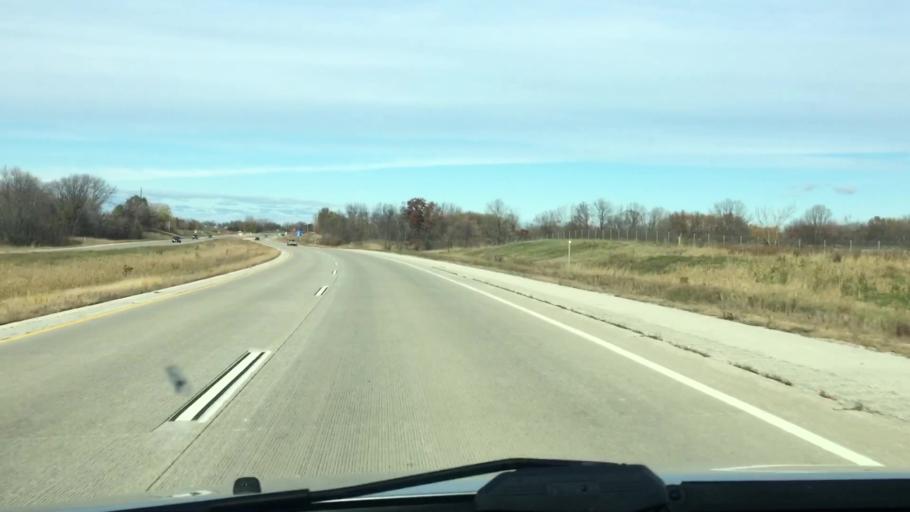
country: US
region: Wisconsin
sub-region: Kewaunee County
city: Luxemburg
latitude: 44.6410
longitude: -87.7532
